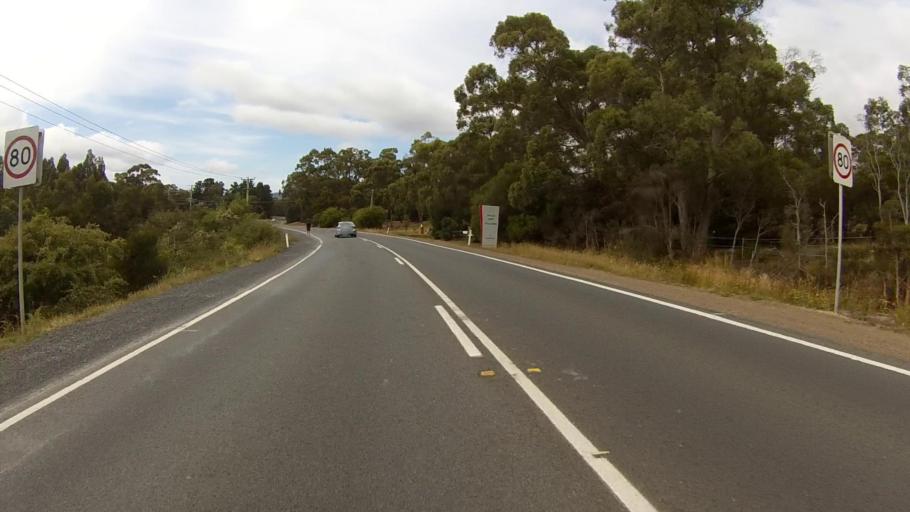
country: AU
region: Tasmania
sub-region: Kingborough
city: Margate
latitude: -43.0382
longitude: 147.2659
